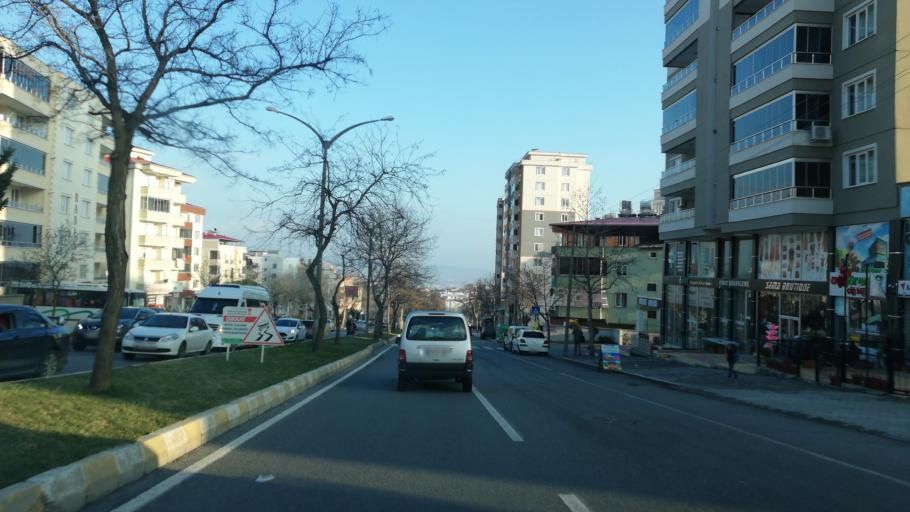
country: TR
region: Kahramanmaras
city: Kahramanmaras
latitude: 37.5921
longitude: 36.8997
